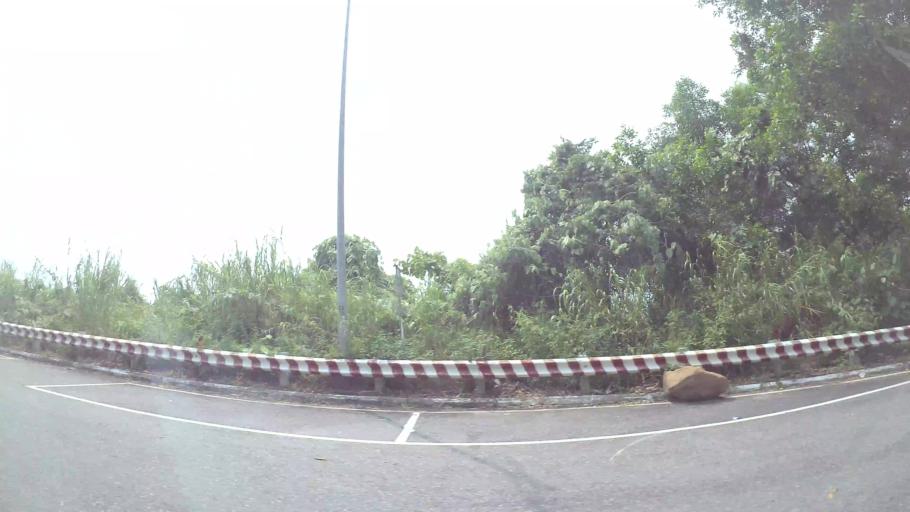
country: VN
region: Da Nang
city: Son Tra
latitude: 16.0992
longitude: 108.3040
